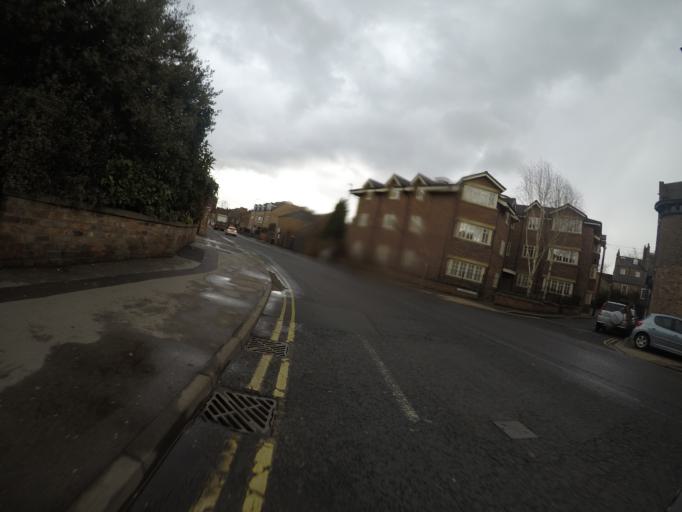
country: GB
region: England
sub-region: City of York
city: York
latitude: 53.9537
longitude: -1.0963
